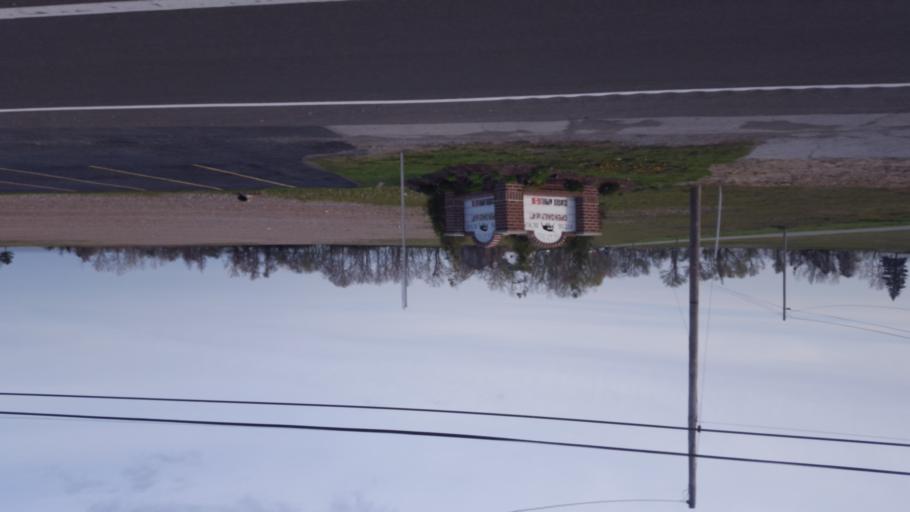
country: US
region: Ohio
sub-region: Erie County
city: Huron
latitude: 41.3782
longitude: -82.4918
